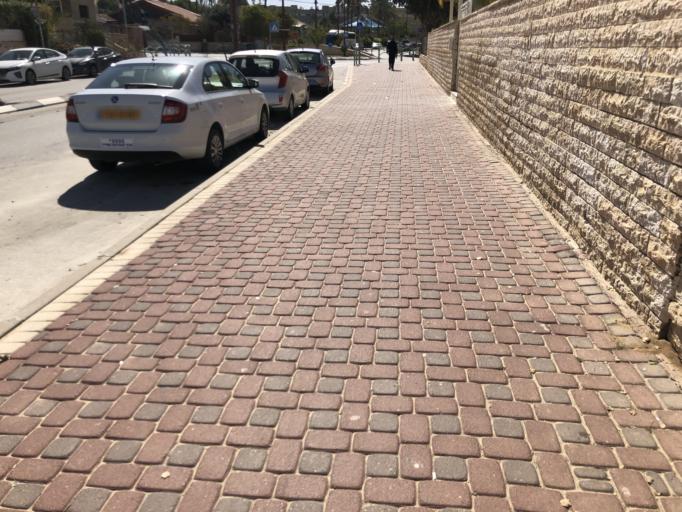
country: IL
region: Southern District
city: Dimona
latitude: 31.0657
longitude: 35.0395
